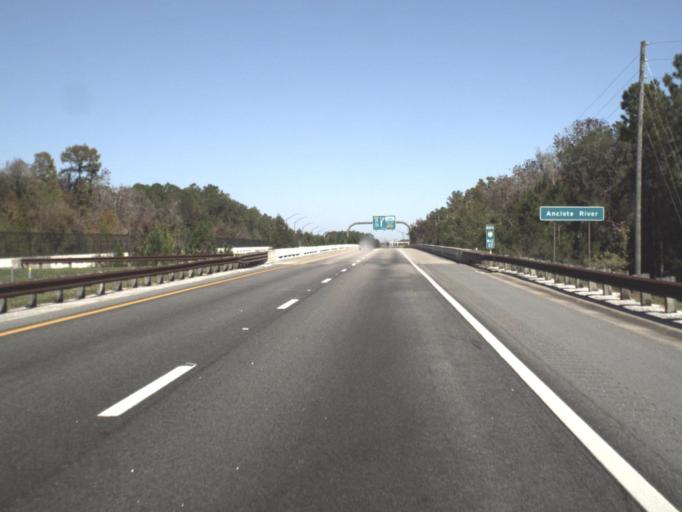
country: US
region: Florida
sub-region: Pasco County
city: Odessa
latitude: 28.2358
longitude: -82.5503
